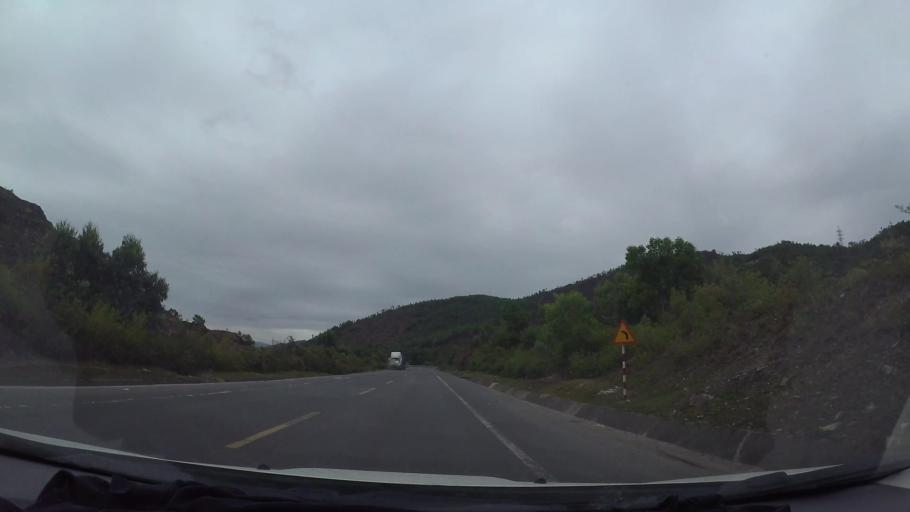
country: VN
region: Da Nang
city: Lien Chieu
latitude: 16.1243
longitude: 108.1000
